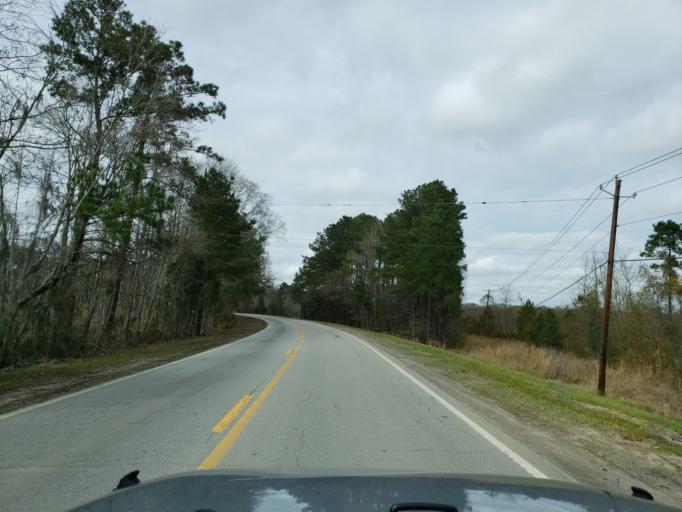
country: US
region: Georgia
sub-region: Chatham County
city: Georgetown
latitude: 32.0352
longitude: -81.2729
